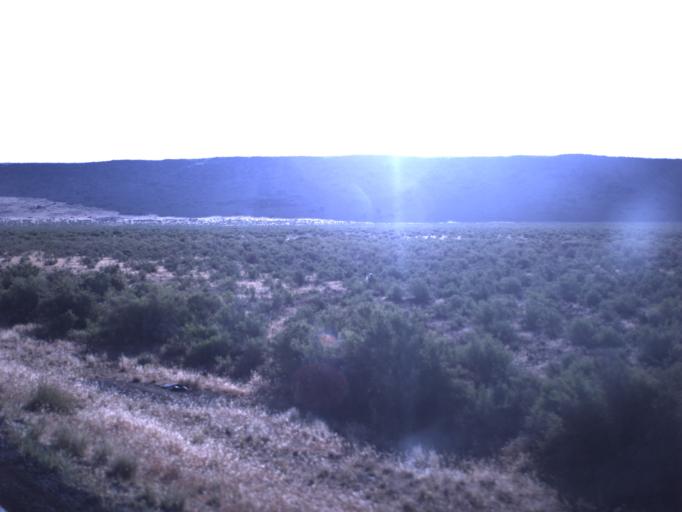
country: US
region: Utah
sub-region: Iron County
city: Enoch
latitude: 37.8407
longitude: -113.0453
